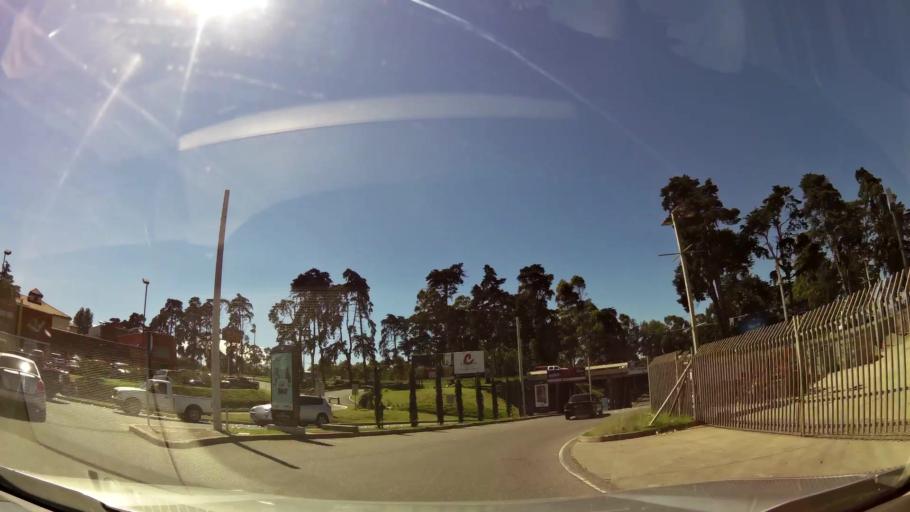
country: GT
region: Guatemala
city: Santa Catarina Pinula
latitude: 14.5542
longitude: -90.4546
